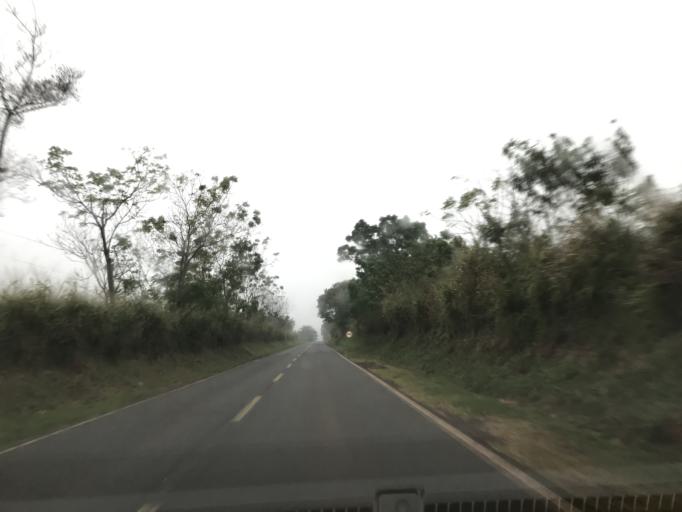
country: PY
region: Canindeyu
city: Salto del Guaira
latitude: -24.1054
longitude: -54.1063
